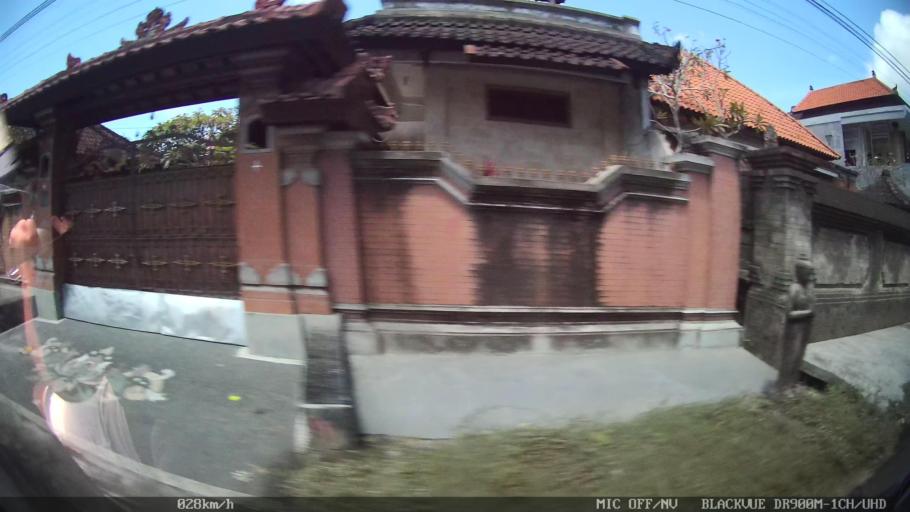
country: ID
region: Bali
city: Banjar Paangkelod
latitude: -8.6121
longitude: 115.2571
